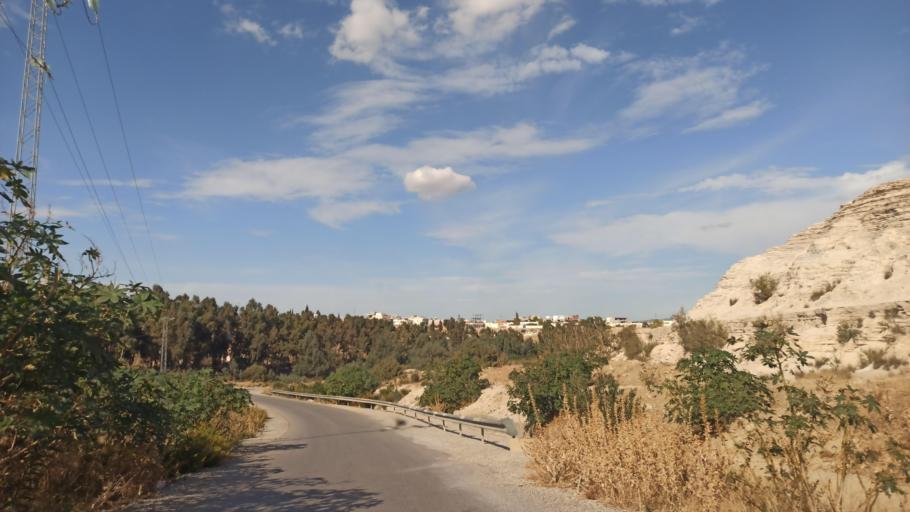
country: TN
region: Zaghwan
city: Zaghouan
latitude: 36.3431
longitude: 10.2077
